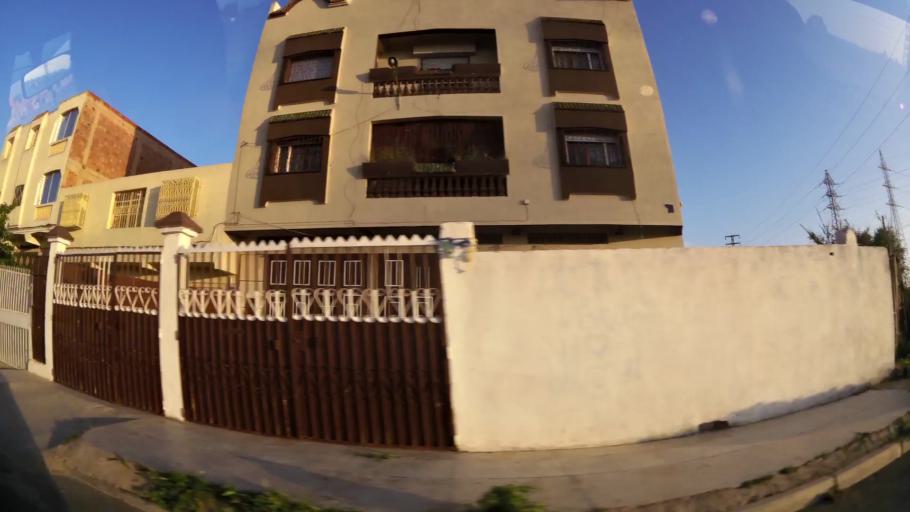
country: MA
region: Oriental
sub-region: Oujda-Angad
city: Oujda
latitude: 34.7094
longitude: -1.9152
